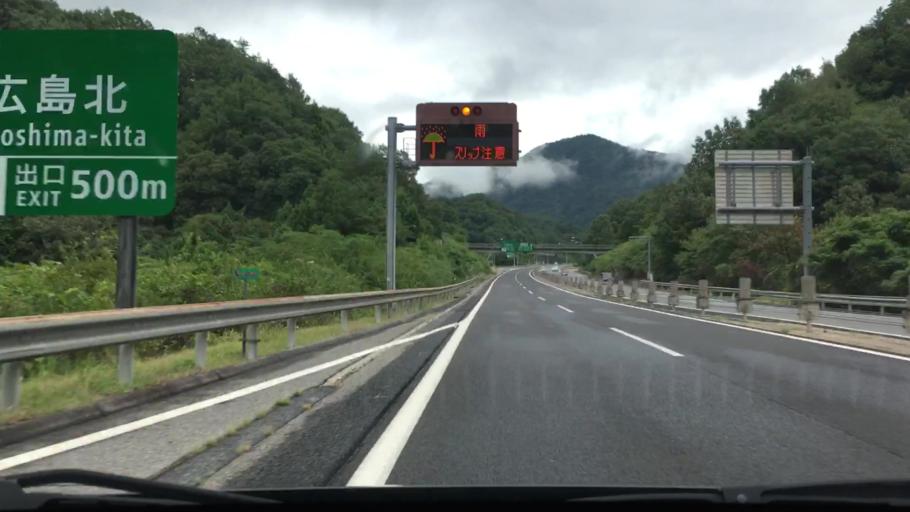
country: JP
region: Hiroshima
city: Hiroshima-shi
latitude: 34.5555
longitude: 132.4508
